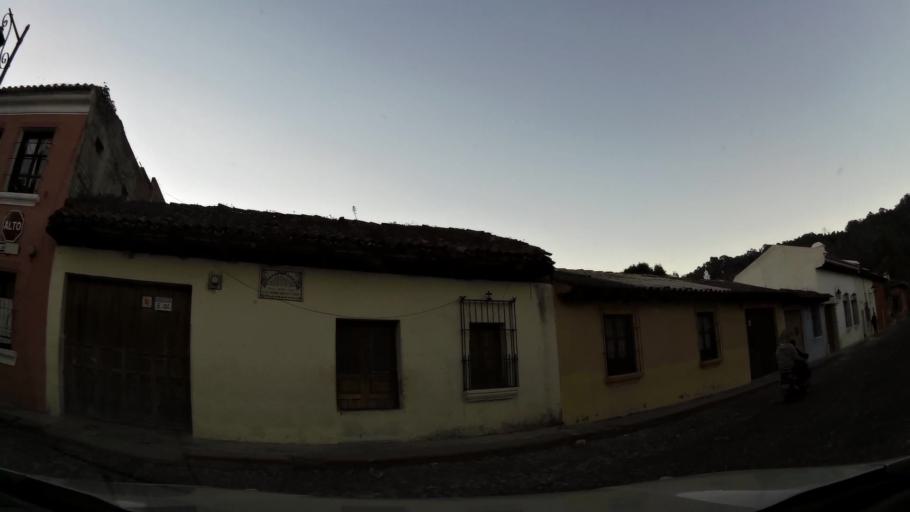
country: GT
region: Sacatepequez
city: Antigua Guatemala
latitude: 14.5603
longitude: -90.7296
